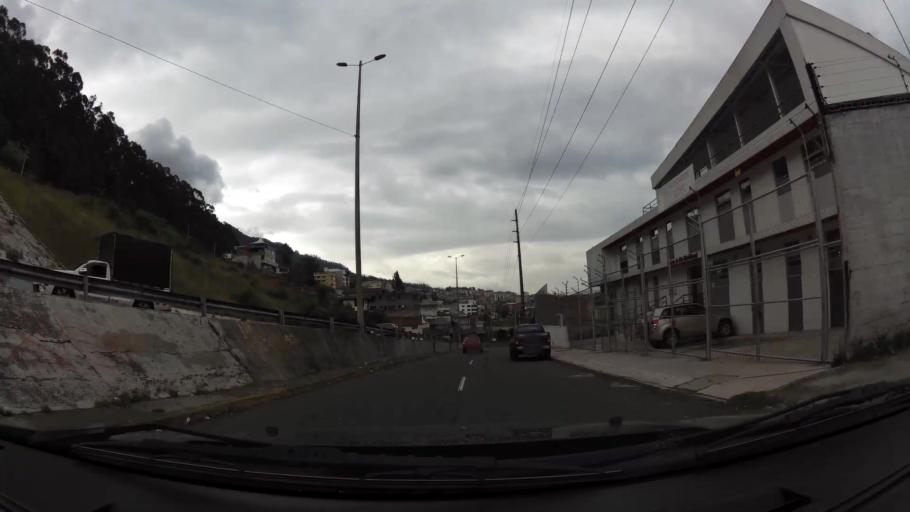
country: EC
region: Pichincha
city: Quito
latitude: -0.1960
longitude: -78.5122
